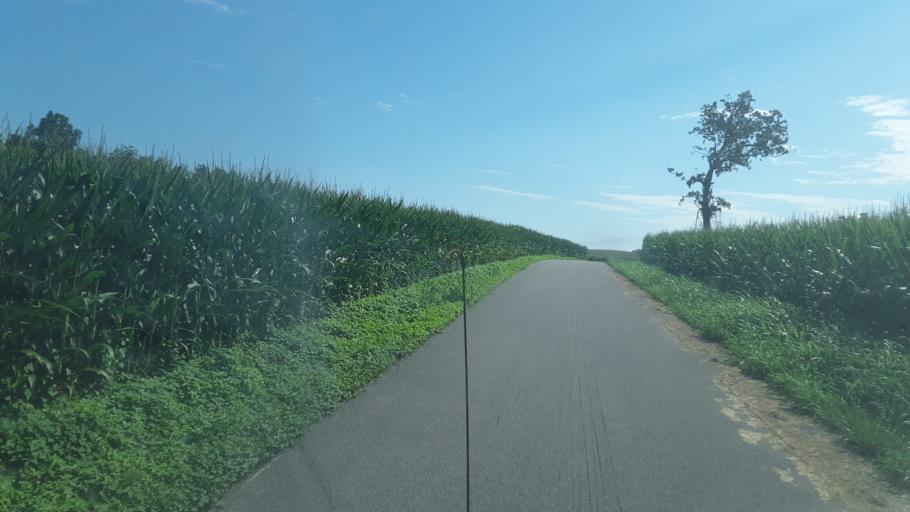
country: US
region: Kentucky
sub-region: Todd County
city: Elkton
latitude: 36.7677
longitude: -87.2286
